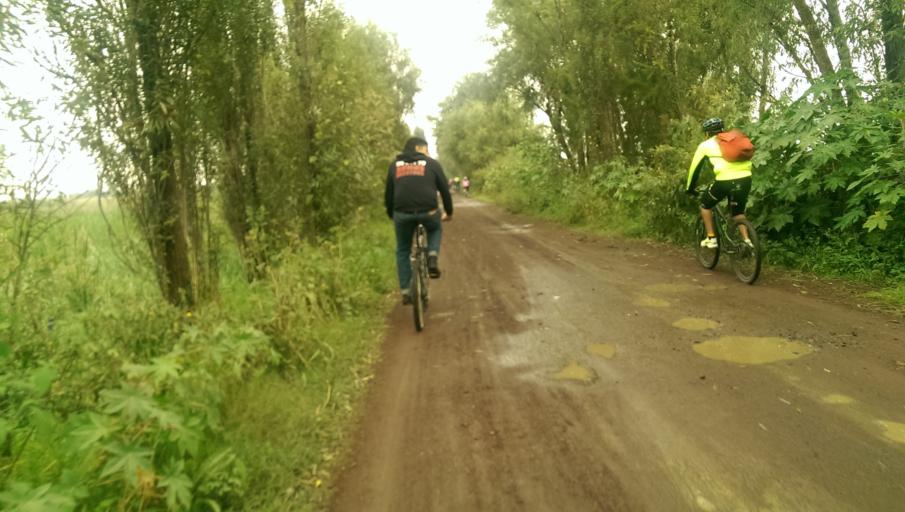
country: MX
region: Mexico City
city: Xochimilco
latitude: 19.2693
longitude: -99.0755
